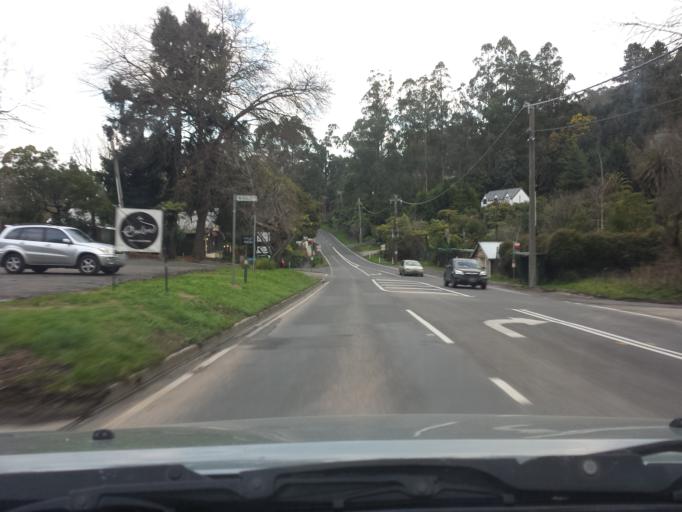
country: AU
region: Victoria
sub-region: Yarra Ranges
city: Belgrave
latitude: -37.9012
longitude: 145.3570
